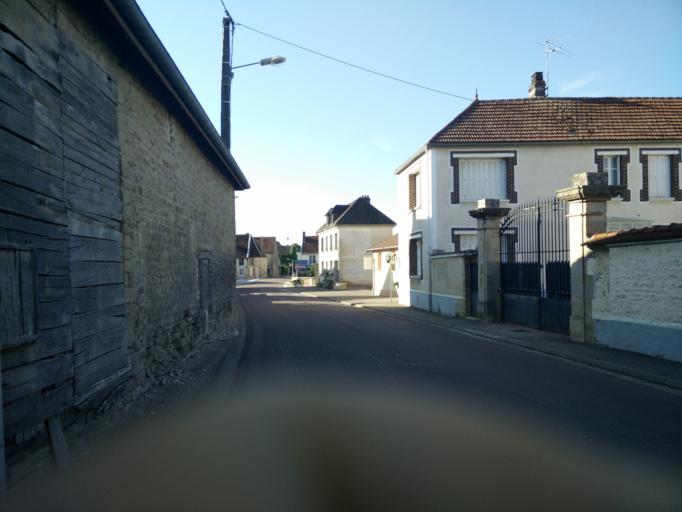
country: FR
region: Champagne-Ardenne
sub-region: Departement de l'Aube
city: Bar-sur-Seine
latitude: 48.0541
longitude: 4.3957
